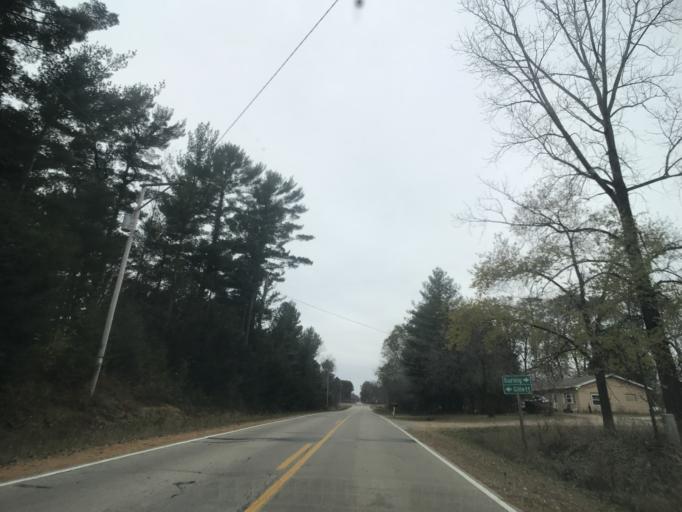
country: US
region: Wisconsin
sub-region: Oconto County
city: Gillett
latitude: 44.9838
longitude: -88.3230
